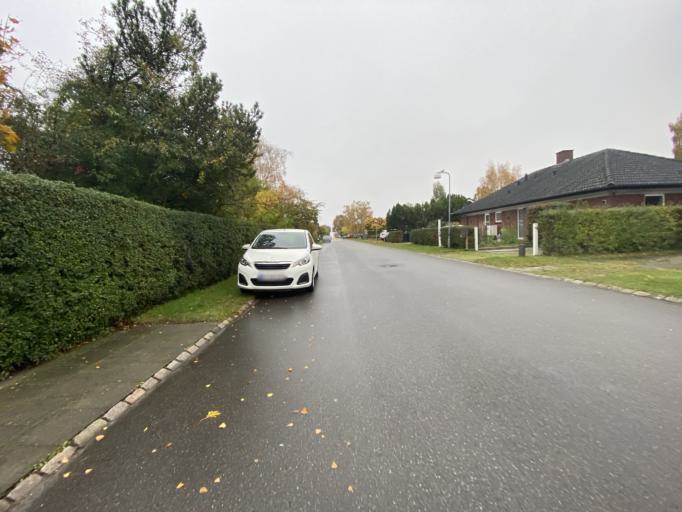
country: DK
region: Capital Region
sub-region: Tarnby Kommune
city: Tarnby
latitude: 55.5687
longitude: 12.6095
